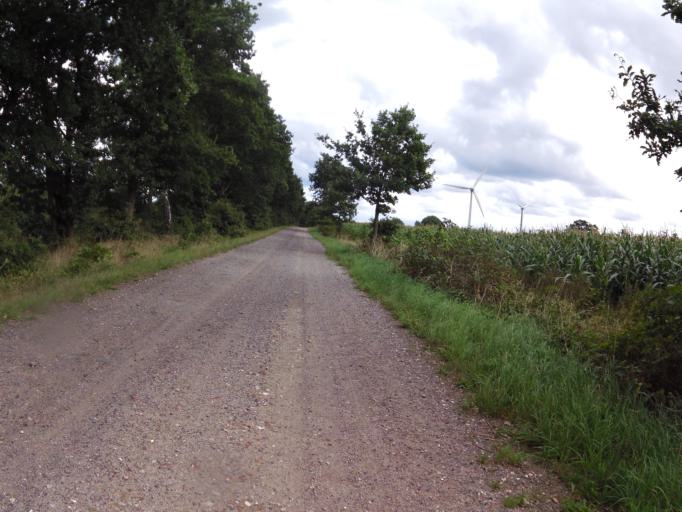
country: DE
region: Lower Saxony
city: Oerel
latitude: 53.4934
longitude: 9.0502
